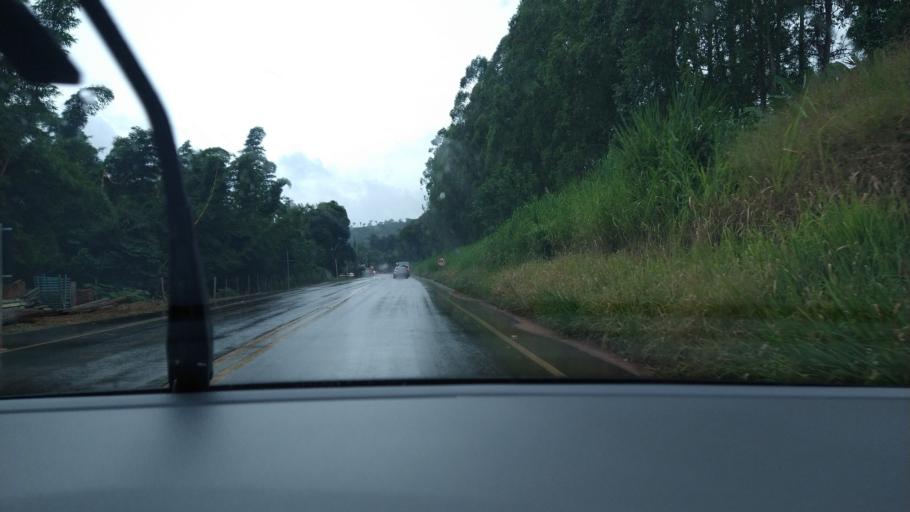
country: BR
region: Minas Gerais
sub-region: Vicosa
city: Vicosa
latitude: -20.6331
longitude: -42.8705
